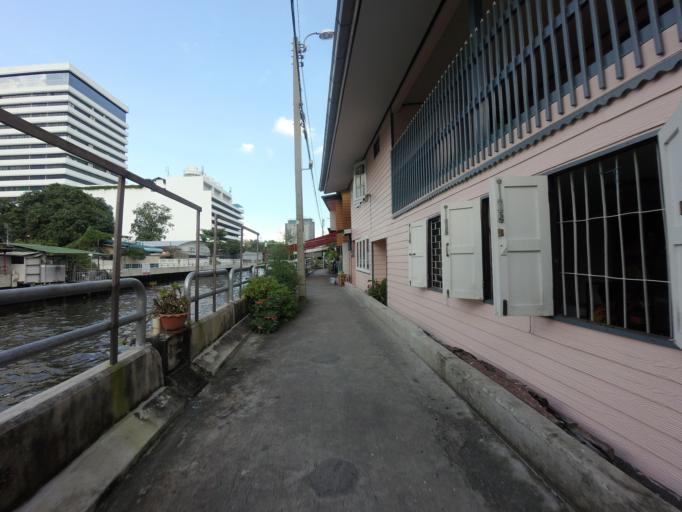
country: TH
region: Bangkok
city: Watthana
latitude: 13.7448
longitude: 100.5783
